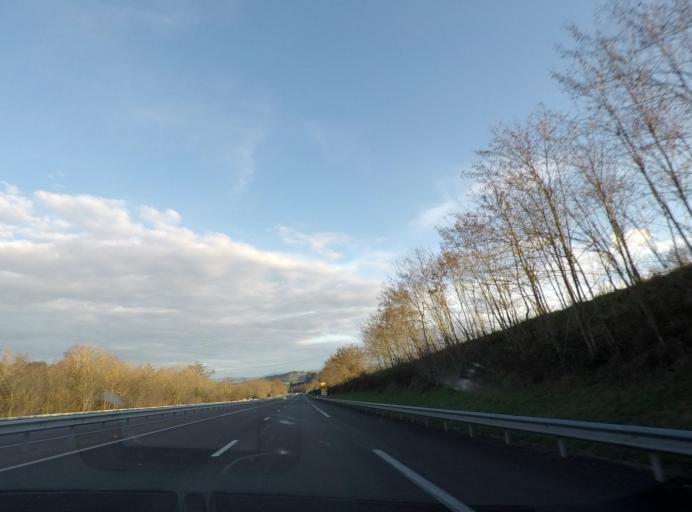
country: FR
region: Bourgogne
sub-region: Departement de Saone-et-Loire
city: Matour
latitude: 46.3843
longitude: 4.4674
